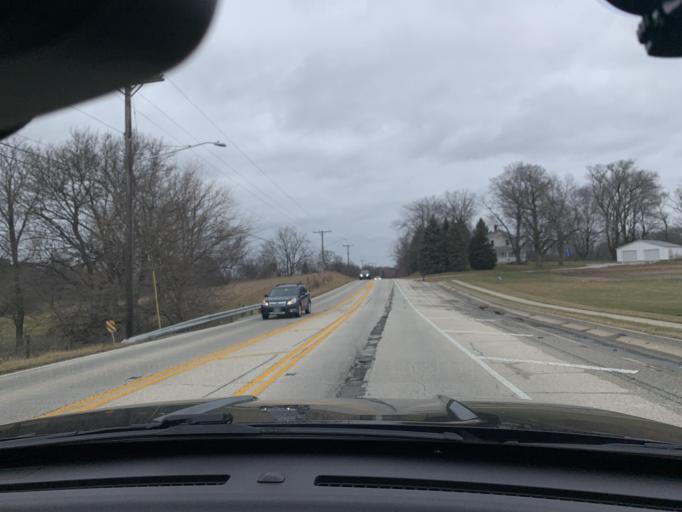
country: US
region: Illinois
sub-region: Sangamon County
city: Jerome
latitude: 39.7241
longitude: -89.6909
